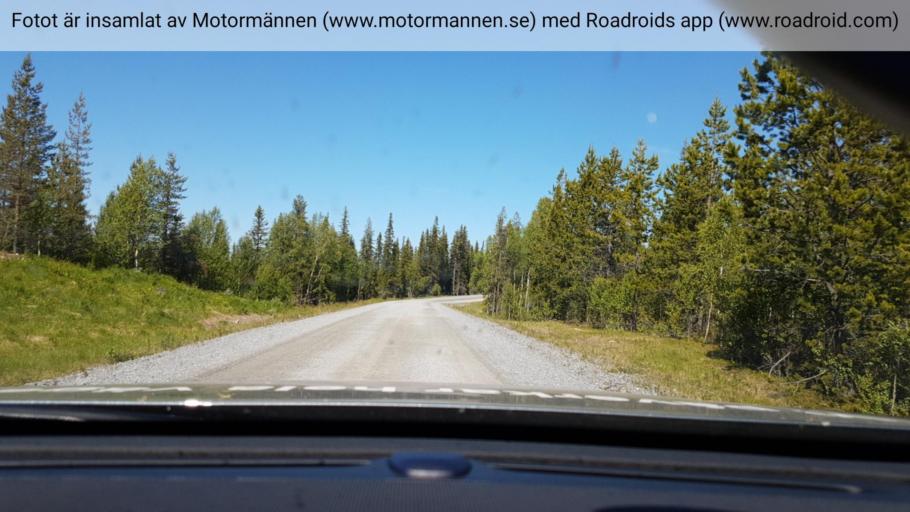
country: SE
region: Vaesterbotten
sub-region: Vilhelmina Kommun
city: Sjoberg
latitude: 64.6797
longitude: 15.7537
